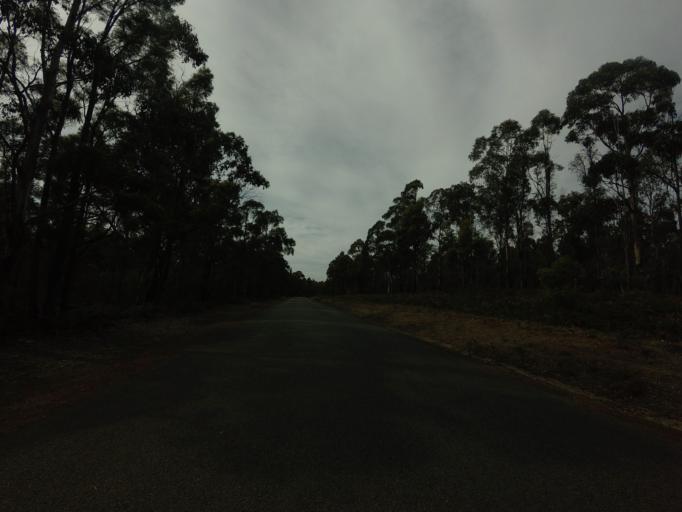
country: AU
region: Tasmania
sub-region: Sorell
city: Sorell
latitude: -42.5160
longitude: 147.6463
